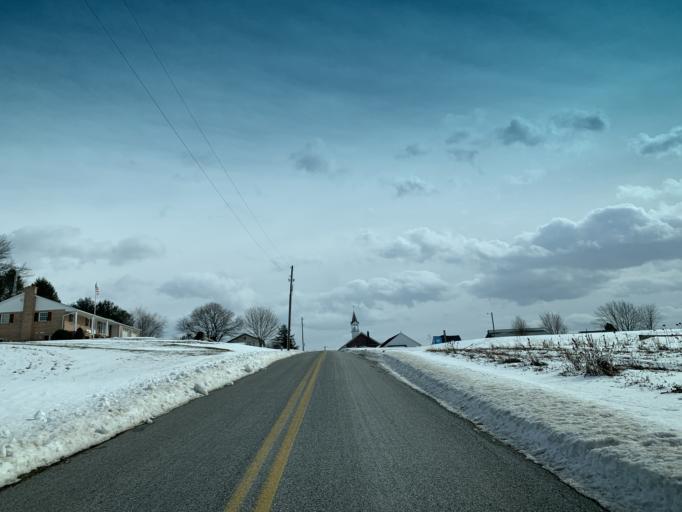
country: US
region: Pennsylvania
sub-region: York County
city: Loganville
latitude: 39.8216
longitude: -76.6753
